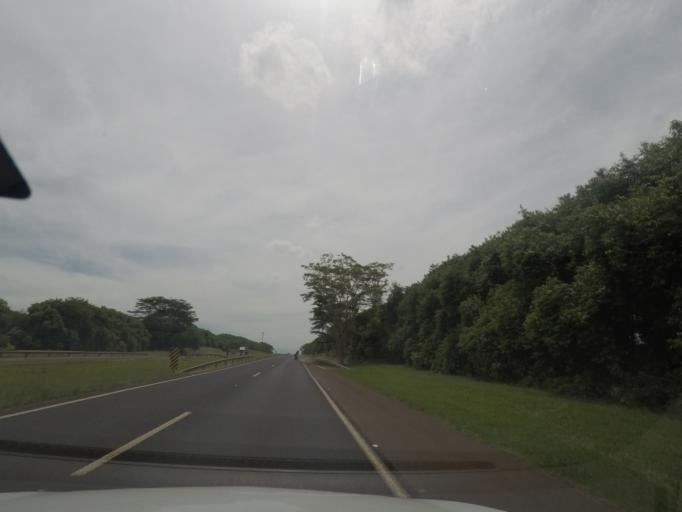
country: BR
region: Sao Paulo
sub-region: Bebedouro
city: Bebedouro
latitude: -20.9972
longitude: -48.4315
